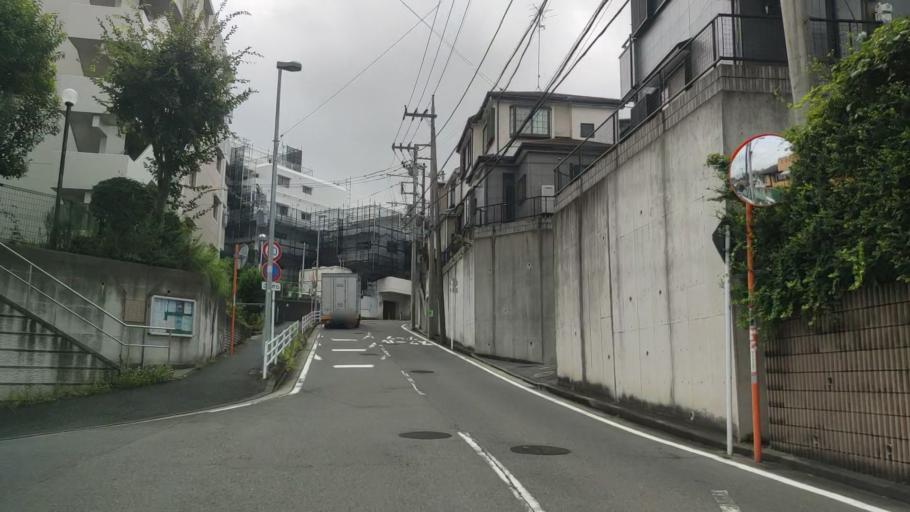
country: JP
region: Kanagawa
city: Minami-rinkan
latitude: 35.4264
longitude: 139.5382
